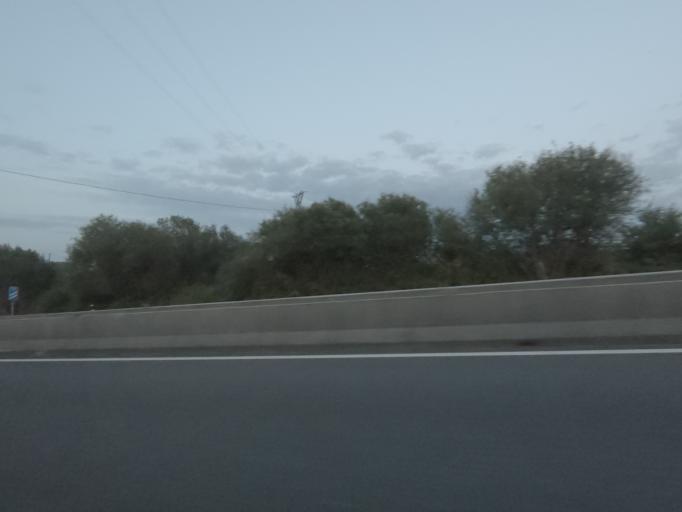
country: ES
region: Galicia
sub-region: Provincia de Pontevedra
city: Tui
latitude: 42.0669
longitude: -8.6463
